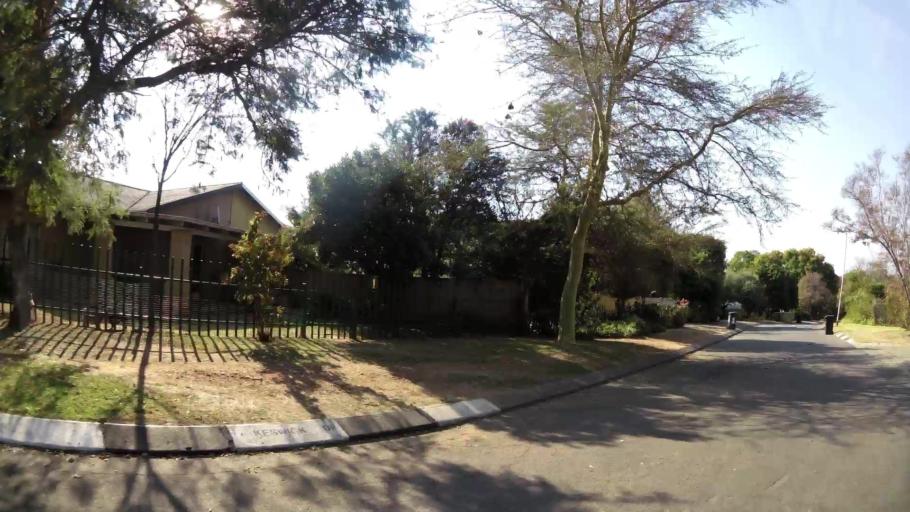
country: ZA
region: Gauteng
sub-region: City of Johannesburg Metropolitan Municipality
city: Modderfontein
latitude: -26.1030
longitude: 28.1479
